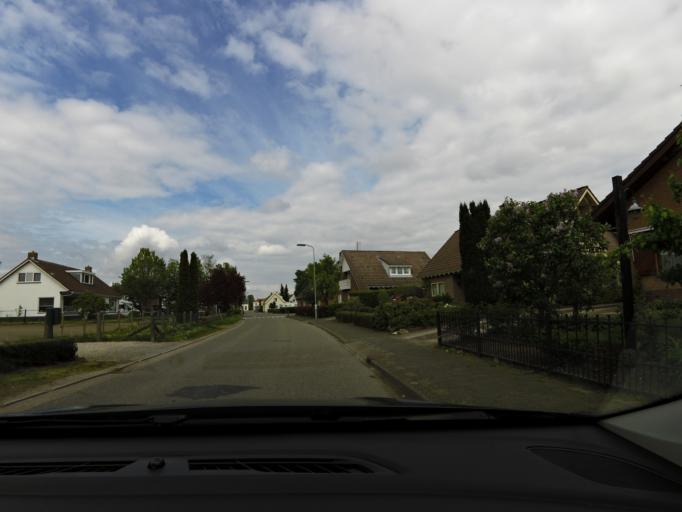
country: NL
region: Gelderland
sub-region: Gemeente Buren
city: Lienden
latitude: 51.9585
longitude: 5.4825
